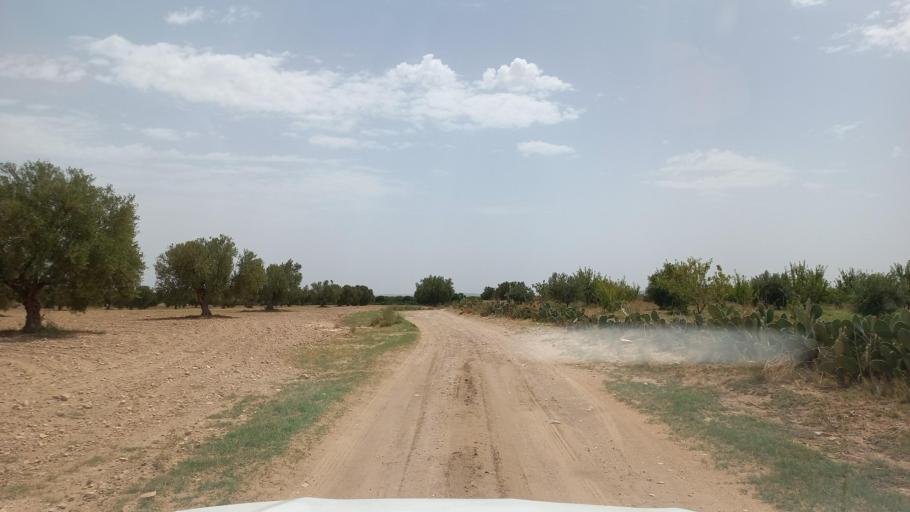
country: TN
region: Al Qasrayn
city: Kasserine
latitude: 35.2921
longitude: 9.0200
